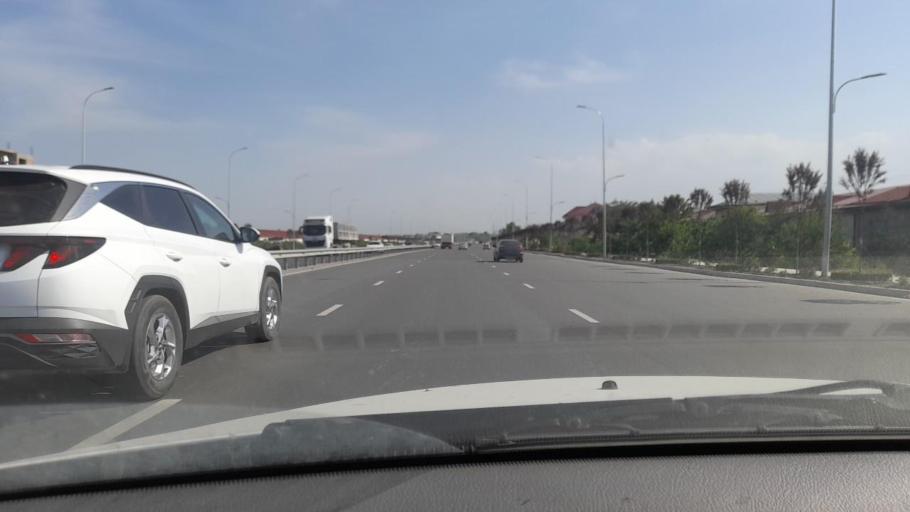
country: UZ
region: Samarqand
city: Daxbet
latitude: 39.7172
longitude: 66.9481
